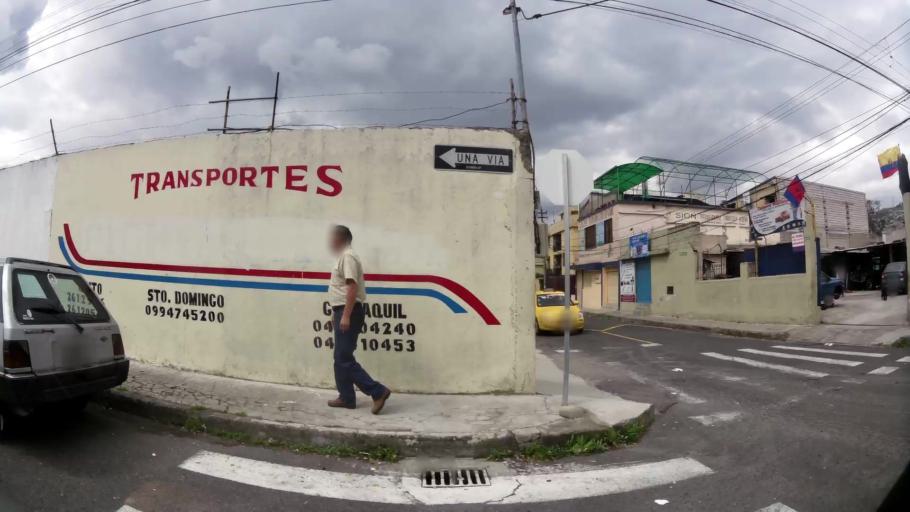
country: EC
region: Pichincha
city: Quito
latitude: -0.2506
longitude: -78.5271
